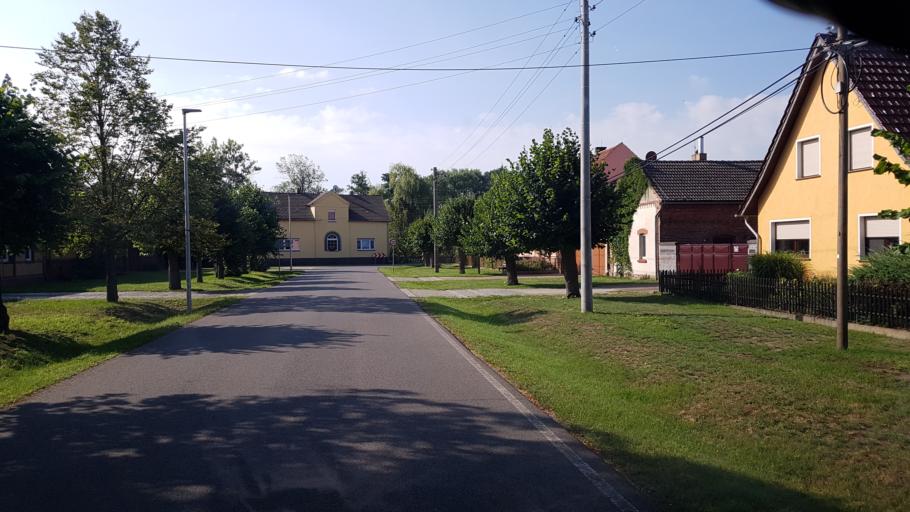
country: DE
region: Brandenburg
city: Luebben
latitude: 51.8671
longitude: 13.8570
